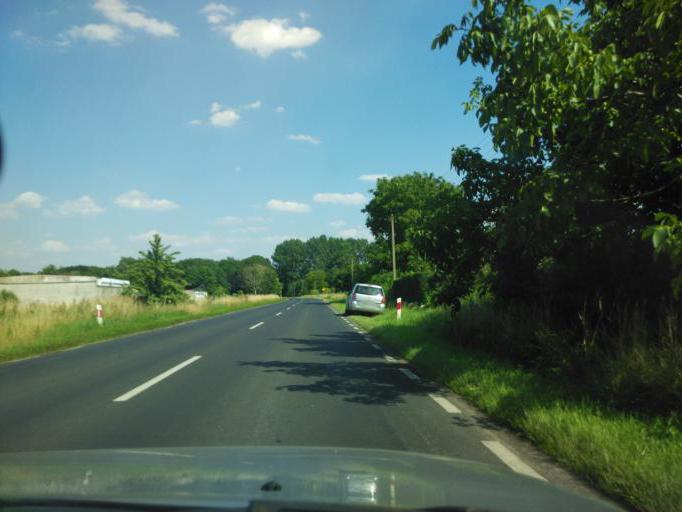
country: PL
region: West Pomeranian Voivodeship
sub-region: Powiat pyrzycki
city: Pyrzyce
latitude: 53.1363
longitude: 14.9172
